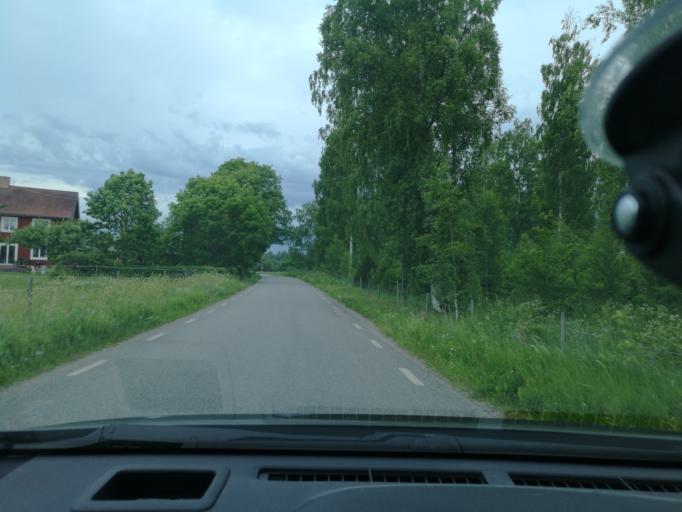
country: SE
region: Vaestmanland
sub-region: Vasteras
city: Skultuna
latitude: 59.8775
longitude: 16.3492
